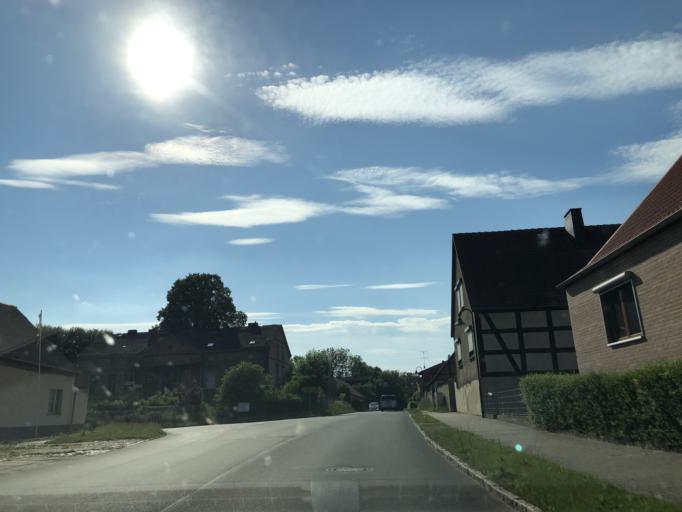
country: DE
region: Brandenburg
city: Angermunde
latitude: 53.0868
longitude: 13.9483
